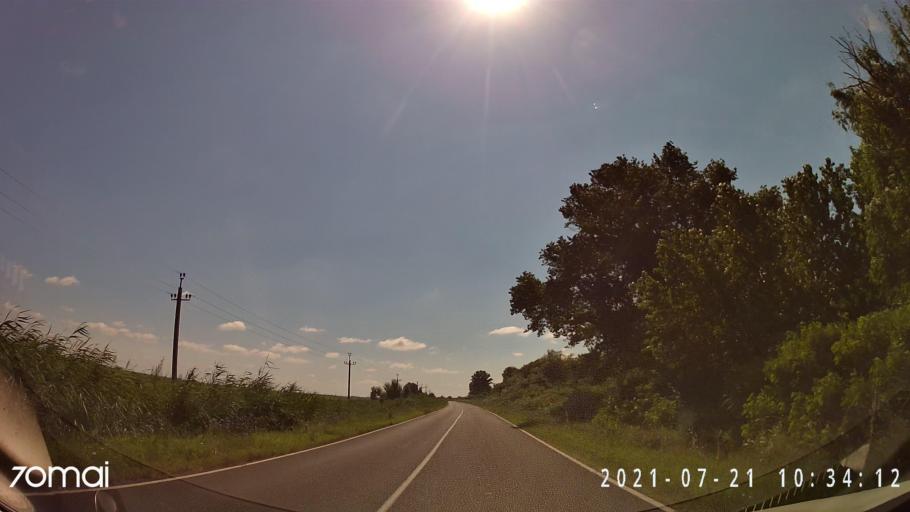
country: RO
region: Tulcea
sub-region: Oras Isaccea
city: Isaccea
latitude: 45.2963
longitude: 28.4424
